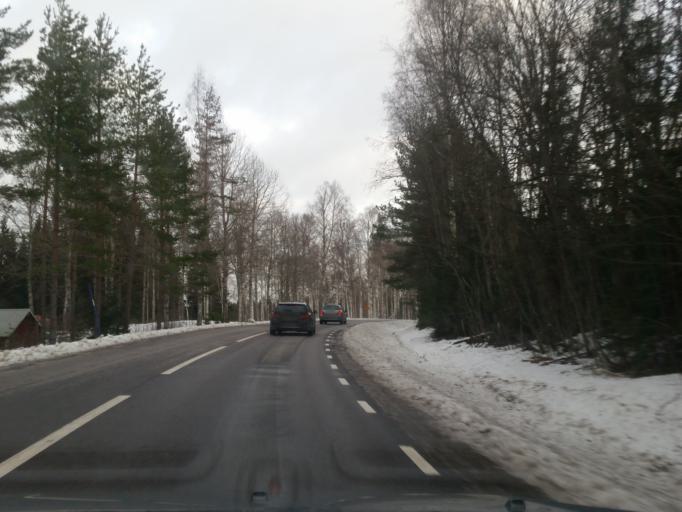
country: SE
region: Gaevleborg
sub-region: Sandvikens Kommun
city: Jarbo
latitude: 60.7530
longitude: 16.5341
